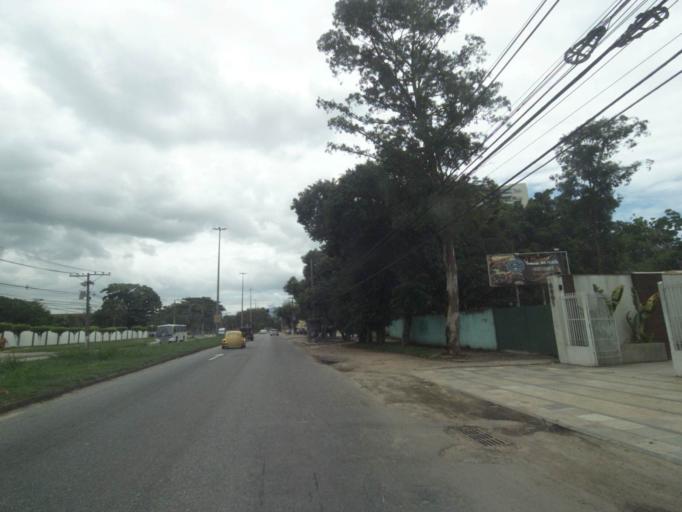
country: BR
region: Rio de Janeiro
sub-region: Nilopolis
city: Nilopolis
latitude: -22.9622
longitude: -43.3982
